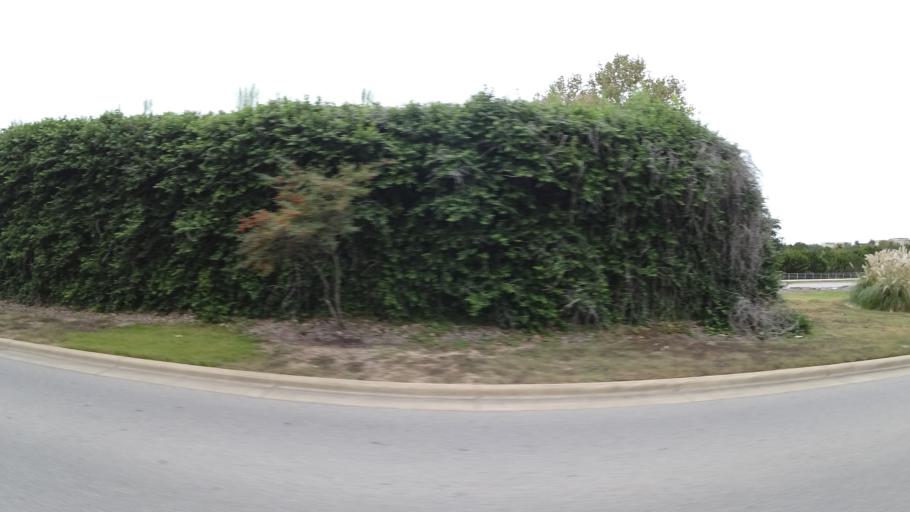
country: US
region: Texas
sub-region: Travis County
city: Hudson Bend
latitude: 30.3851
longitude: -97.8826
